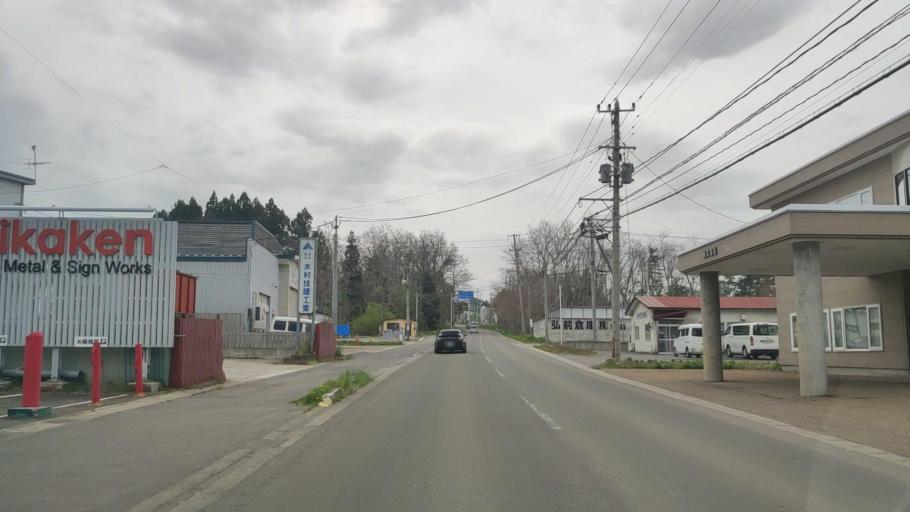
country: JP
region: Aomori
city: Aomori Shi
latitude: 40.7774
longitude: 140.7944
